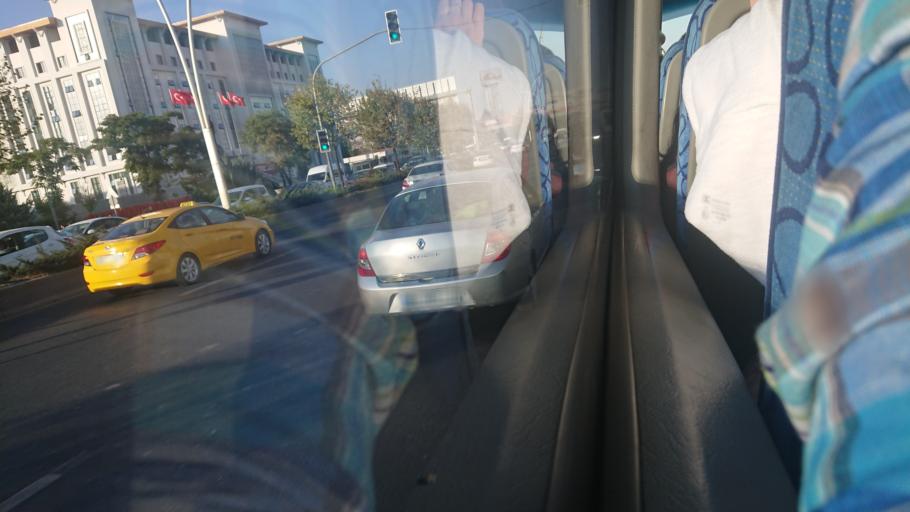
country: TR
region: Ankara
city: Ankara
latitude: 39.9468
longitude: 32.8313
